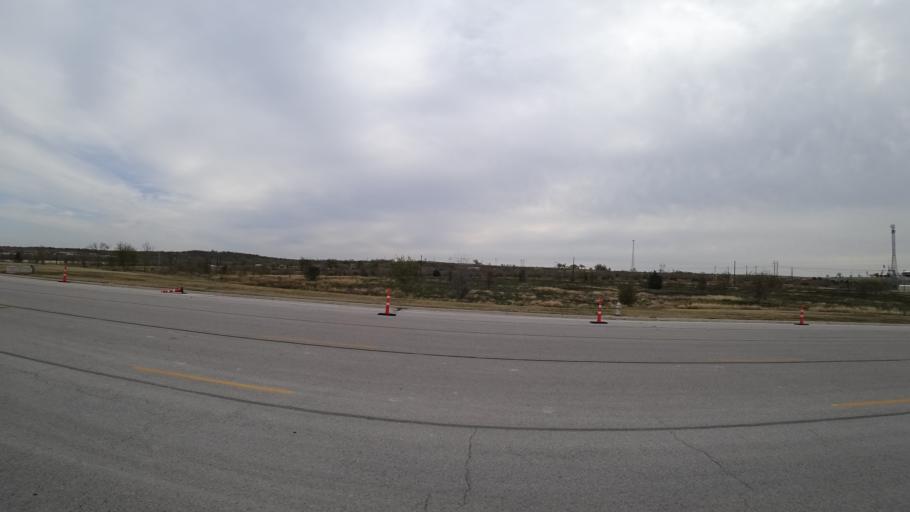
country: US
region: Texas
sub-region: Travis County
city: Garfield
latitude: 30.1439
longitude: -97.6251
